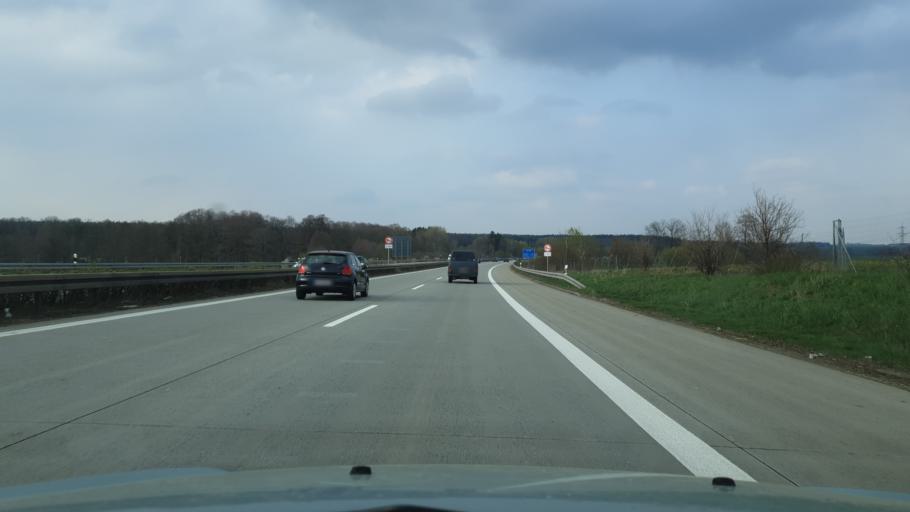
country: DE
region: Saxony
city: Niederdorf
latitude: 50.7337
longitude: 12.7804
